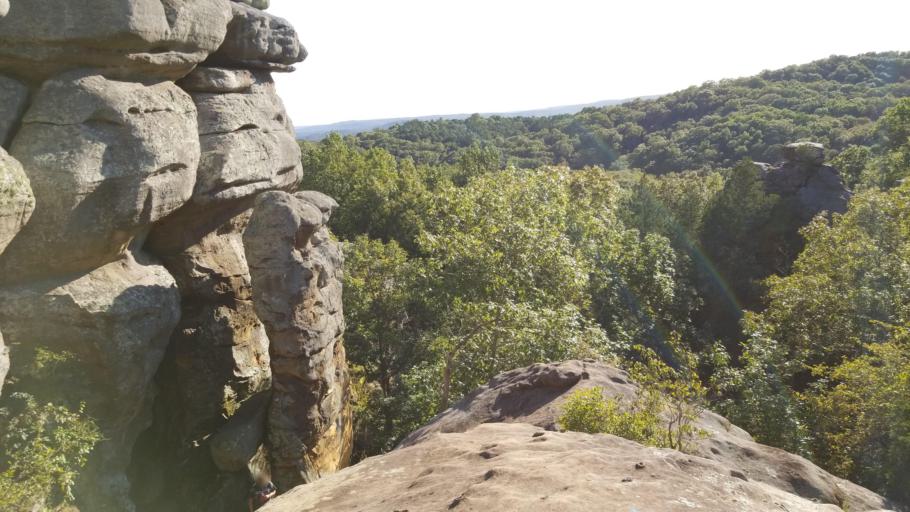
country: US
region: Illinois
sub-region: Hardin County
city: Elizabethtown
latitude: 37.6038
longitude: -88.3859
